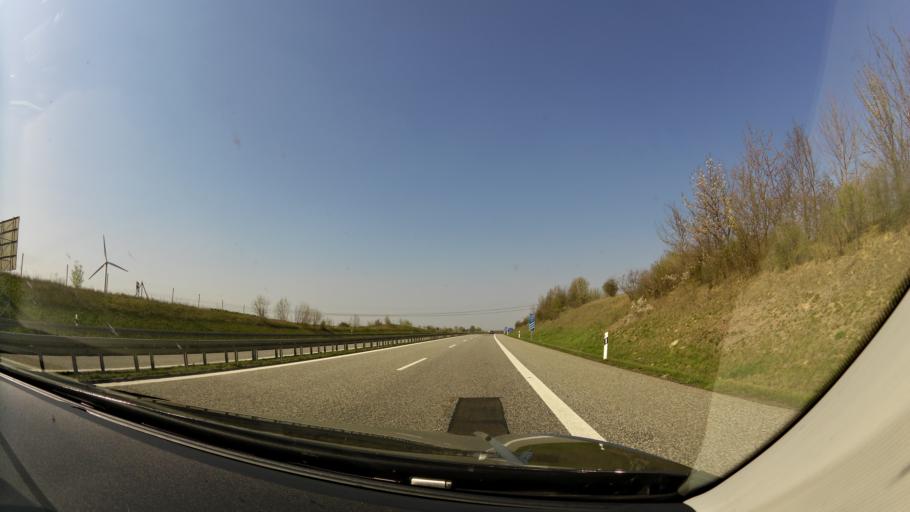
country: DE
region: Brandenburg
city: Schonfeld
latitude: 53.4582
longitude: 13.9695
